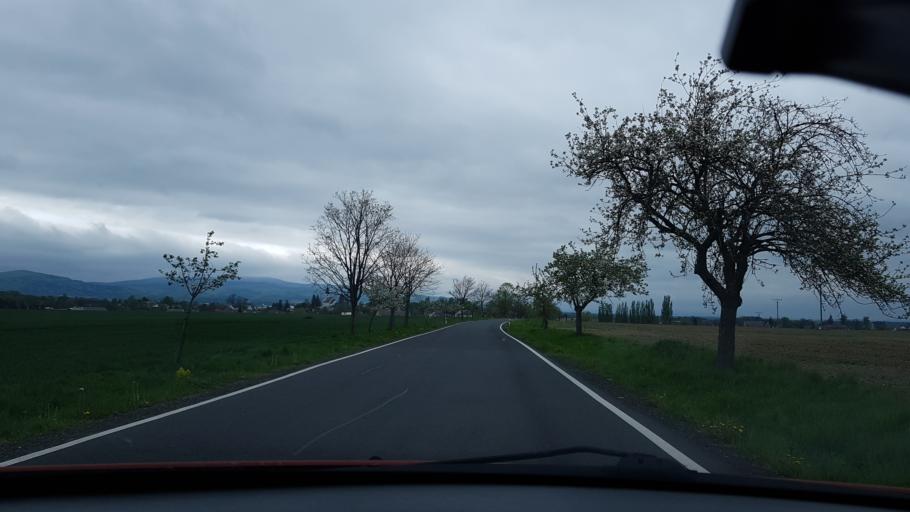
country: CZ
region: Olomoucky
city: Zulova
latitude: 50.3863
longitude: 17.0910
